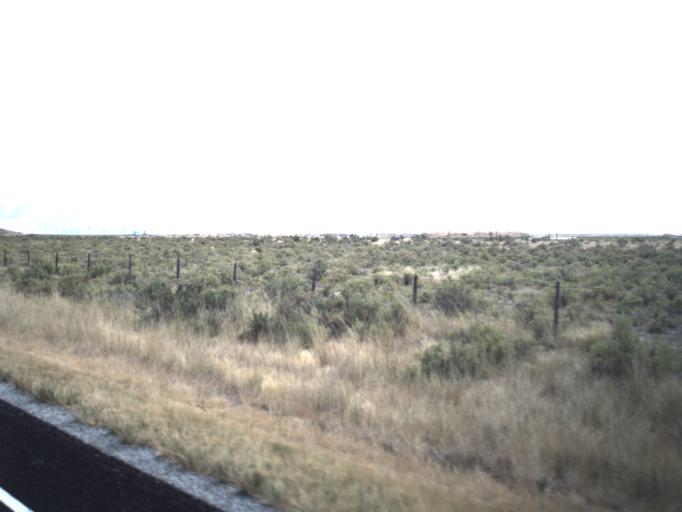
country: US
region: Utah
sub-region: Box Elder County
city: Tremonton
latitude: 41.6269
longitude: -112.3991
